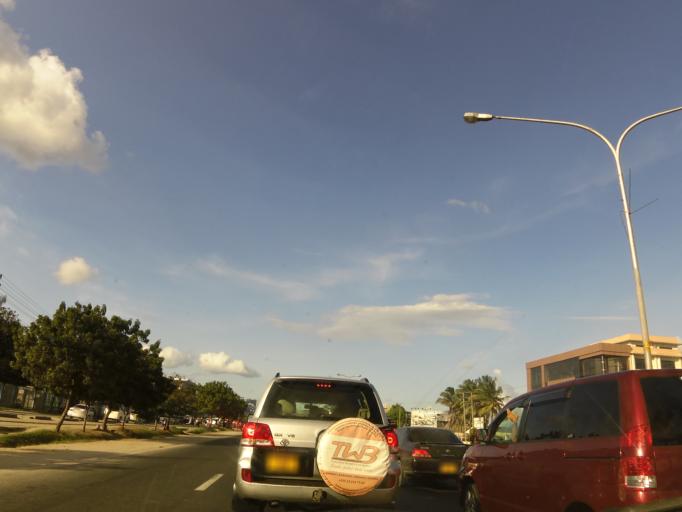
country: TZ
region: Dar es Salaam
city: Dar es Salaam
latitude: -6.8520
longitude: 39.2294
